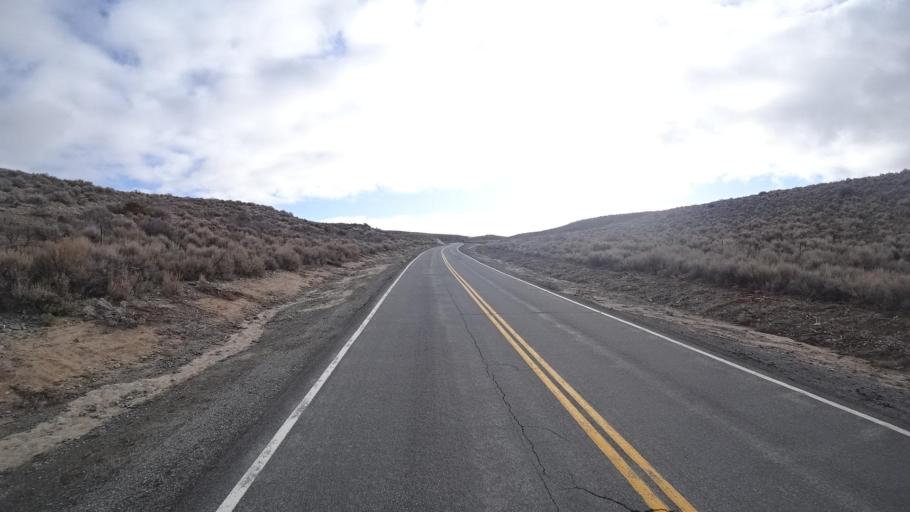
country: US
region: Nevada
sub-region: Washoe County
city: Cold Springs
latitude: 39.8043
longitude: -119.9244
